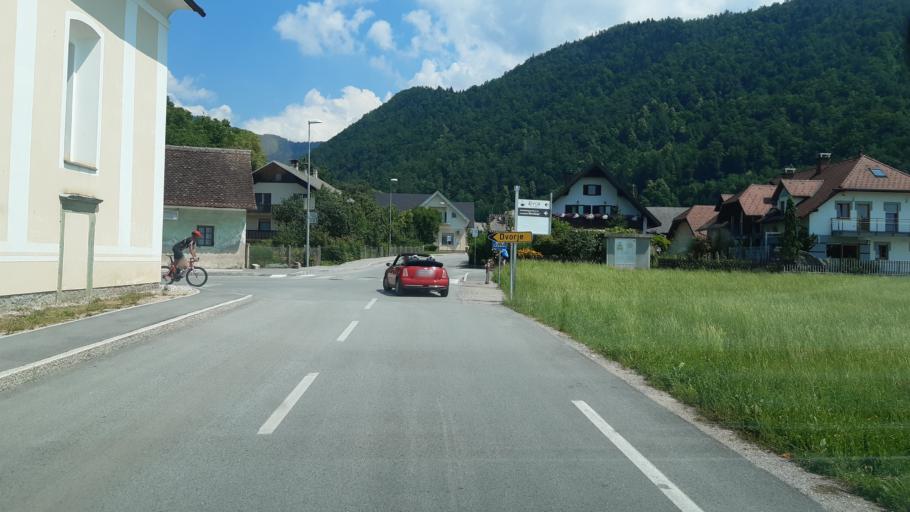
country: SI
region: Cerklje na Gorenjskem
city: Cerklje na Gorenjskem
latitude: 46.2606
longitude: 14.4919
